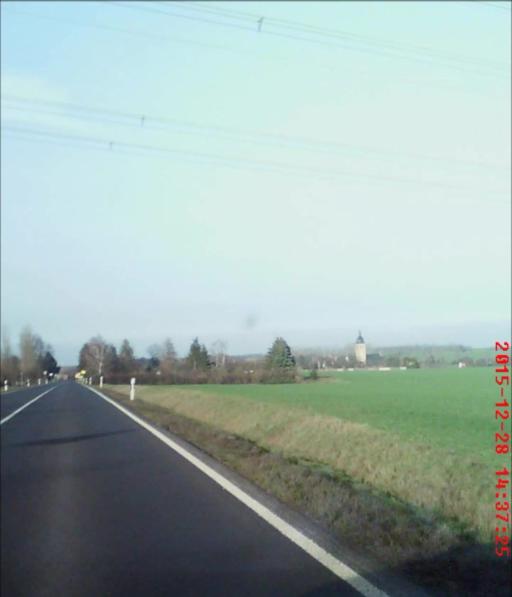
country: DE
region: Thuringia
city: Buttelstedt
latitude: 51.0653
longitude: 11.3405
